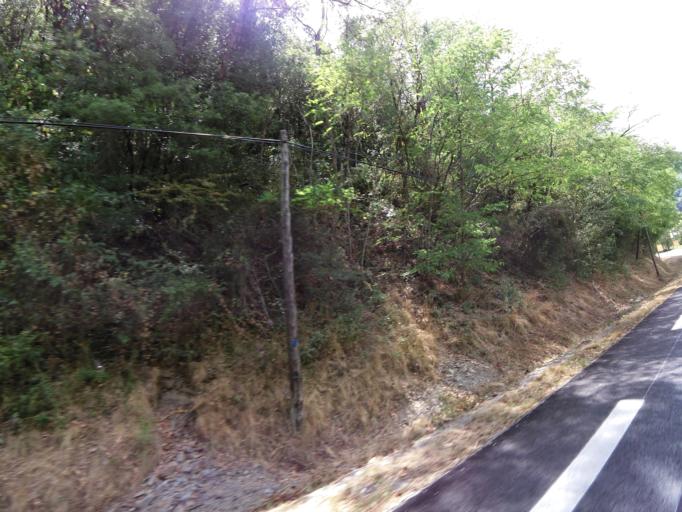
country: FR
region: Languedoc-Roussillon
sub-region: Departement du Gard
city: Sumene
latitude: 43.9776
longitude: 3.6873
